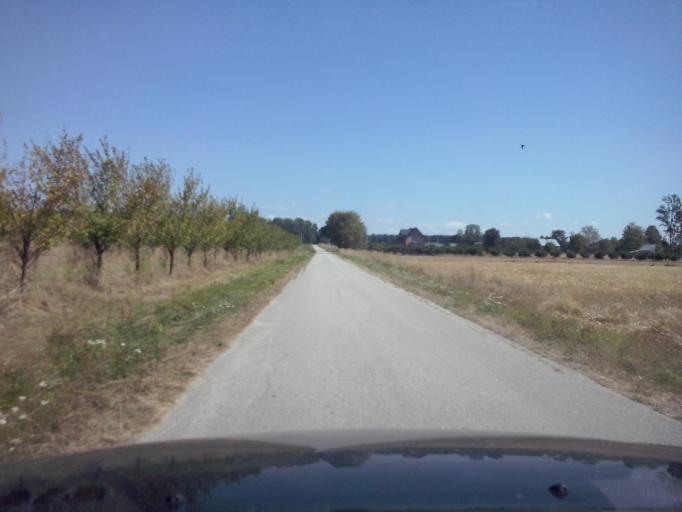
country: PL
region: Swietokrzyskie
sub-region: Powiat buski
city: Gnojno
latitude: 50.6043
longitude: 20.9190
